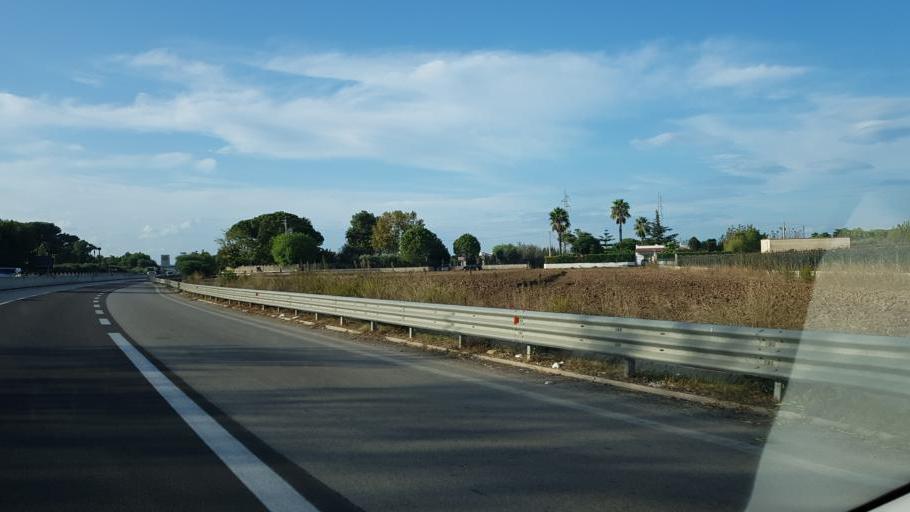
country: IT
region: Apulia
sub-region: Provincia di Brindisi
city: Francavilla Fontana
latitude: 40.5328
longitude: 17.6181
